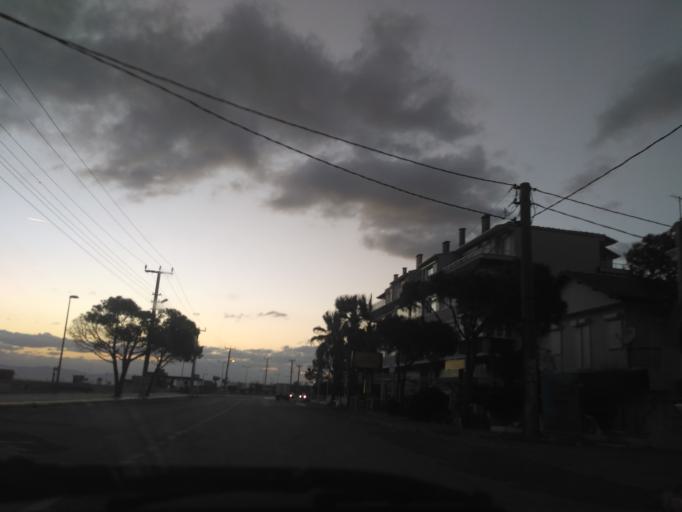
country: TR
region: Balikesir
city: Ayvalik
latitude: 39.2690
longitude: 26.6612
